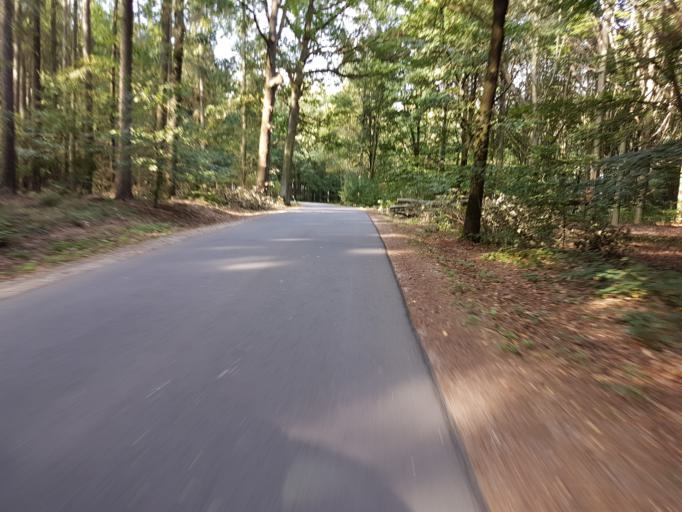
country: DE
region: Saxony
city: Claussnitz
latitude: 50.9524
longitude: 12.8793
